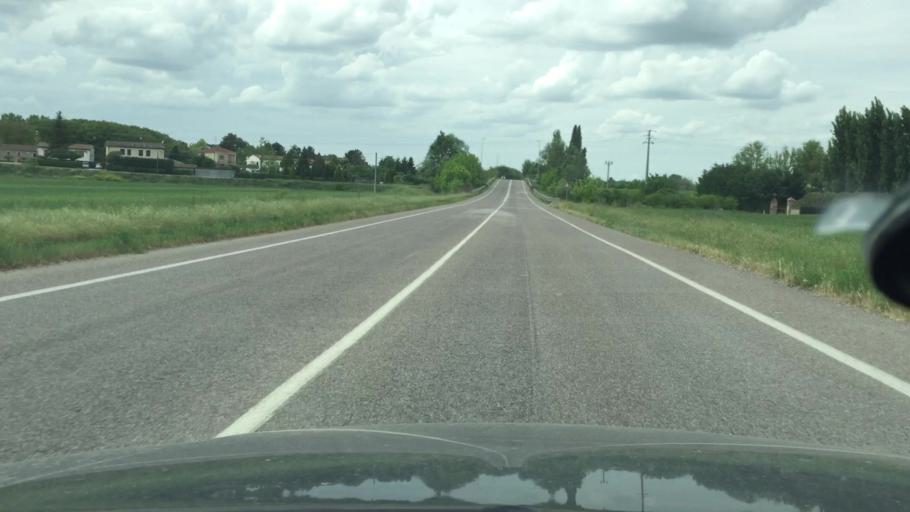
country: IT
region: Emilia-Romagna
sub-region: Provincia di Ferrara
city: Cona
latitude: 44.8103
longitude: 11.7165
